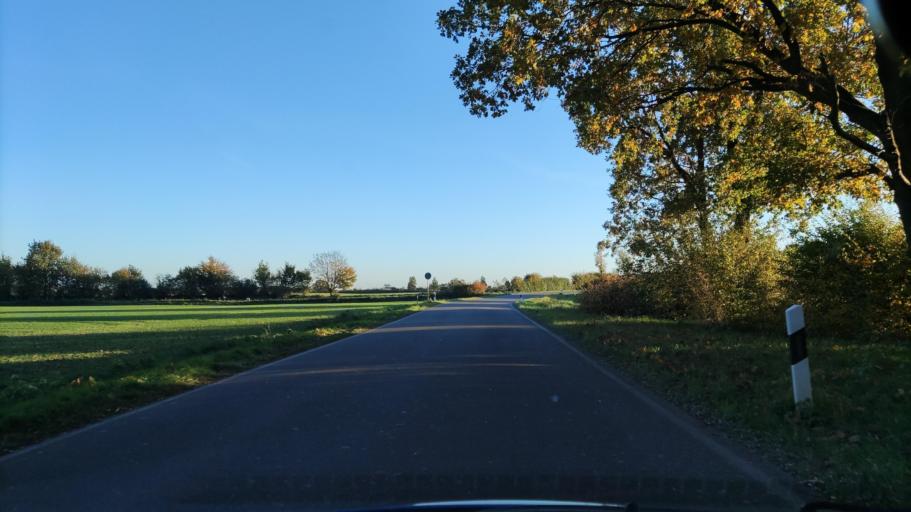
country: DE
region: Schleswig-Holstein
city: Basthorst
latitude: 53.5702
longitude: 10.4734
